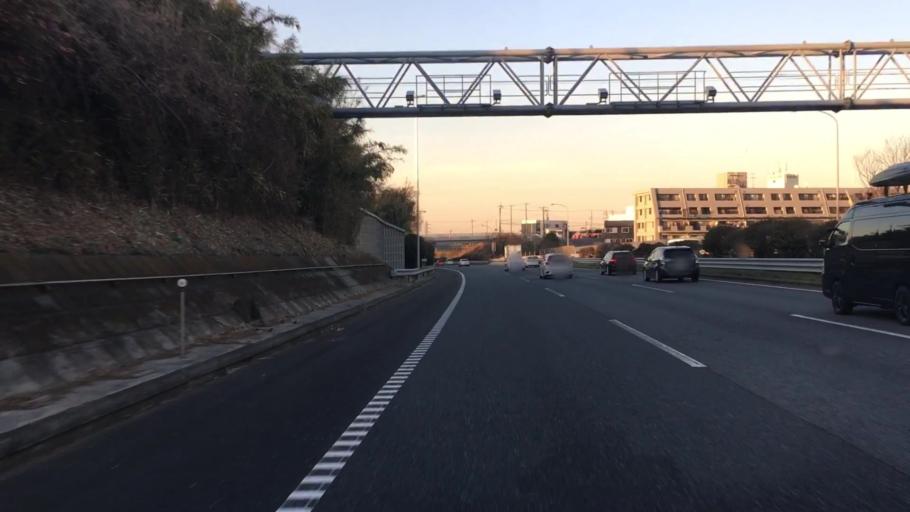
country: JP
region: Kanagawa
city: Yokohama
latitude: 35.4915
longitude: 139.5922
